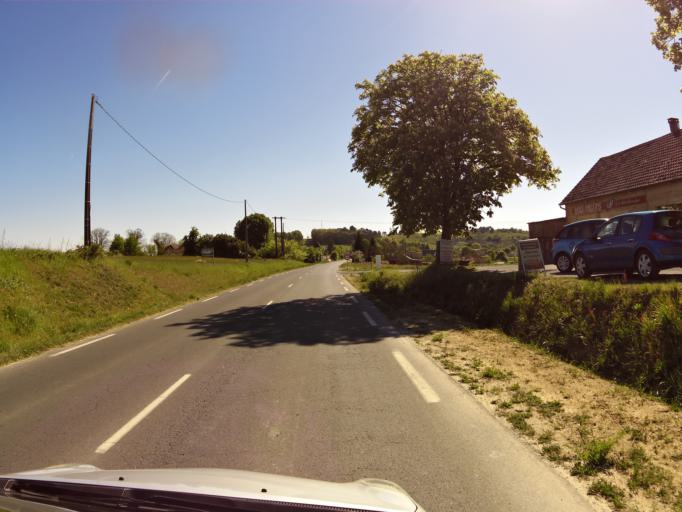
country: FR
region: Aquitaine
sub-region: Departement de la Dordogne
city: Sarlat-la-Caneda
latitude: 44.9337
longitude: 1.2093
